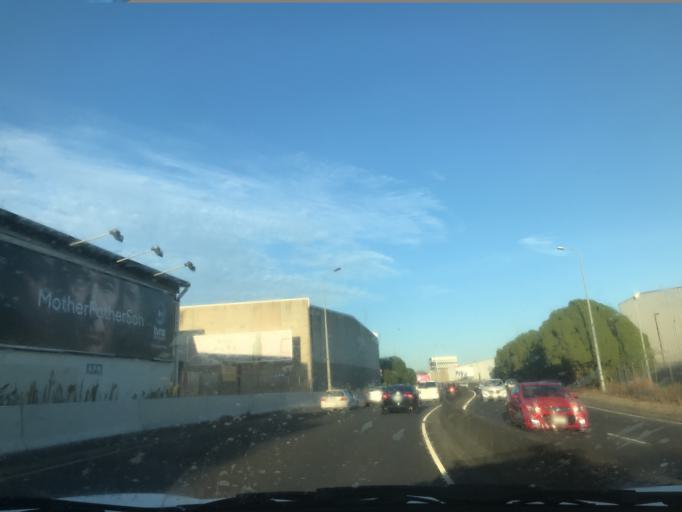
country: NZ
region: Auckland
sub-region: Auckland
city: Tamaki
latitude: -36.9143
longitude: 174.8509
